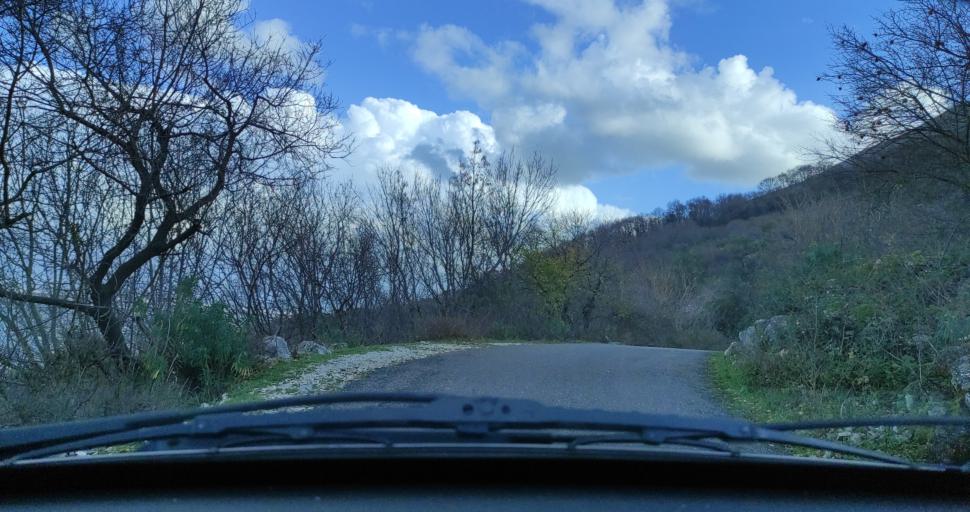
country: AL
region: Shkoder
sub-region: Rrethi i Shkodres
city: Dajc
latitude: 42.0700
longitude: 19.4057
